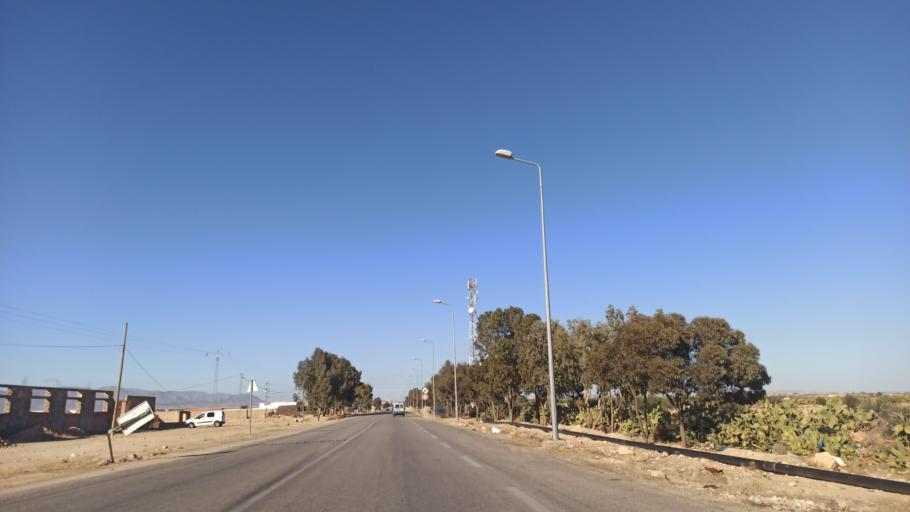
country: TN
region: Sidi Bu Zayd
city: Jilma
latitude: 35.2903
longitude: 9.4181
